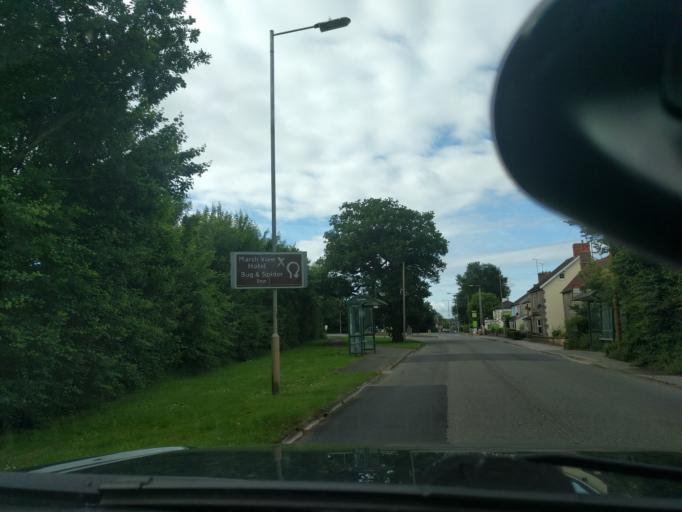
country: GB
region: England
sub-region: Wiltshire
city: Calne
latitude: 51.4478
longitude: -1.9954
